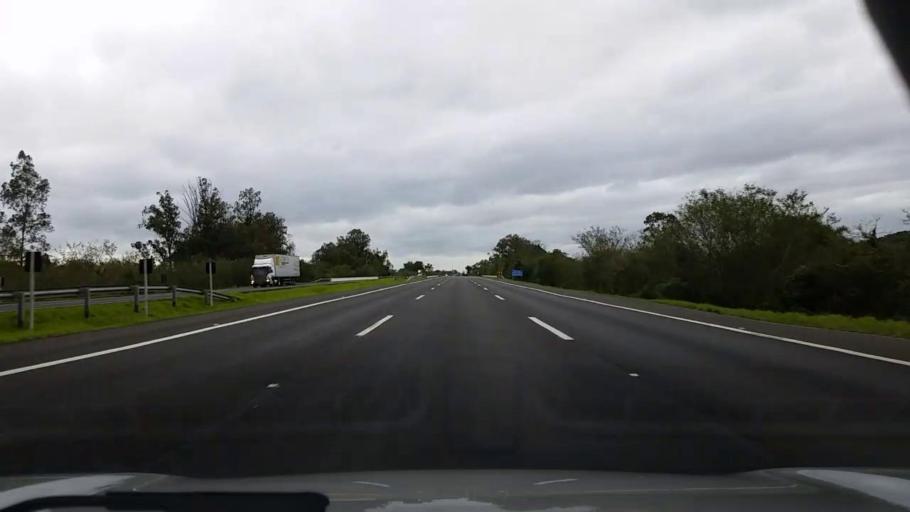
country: BR
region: Rio Grande do Sul
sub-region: Rolante
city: Rolante
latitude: -29.8834
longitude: -50.5478
